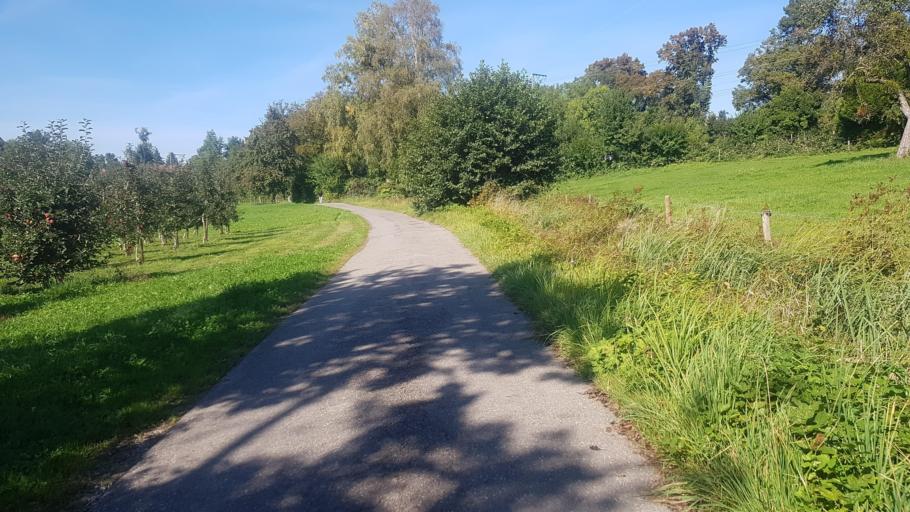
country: DE
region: Bavaria
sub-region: Swabia
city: Lindau
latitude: 47.5613
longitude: 9.6819
